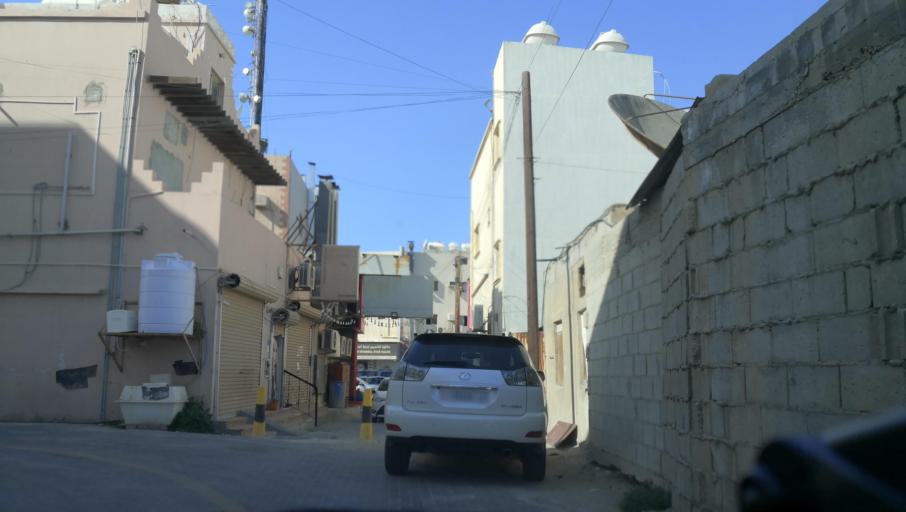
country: BH
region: Muharraq
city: Al Muharraq
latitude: 26.2548
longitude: 50.6323
